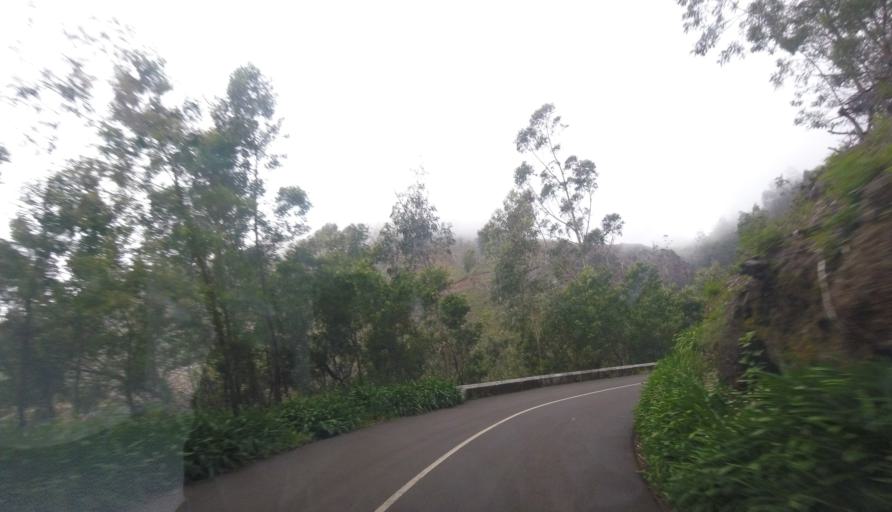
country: PT
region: Madeira
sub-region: Funchal
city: Nossa Senhora do Monte
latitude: 32.6920
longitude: -16.8955
